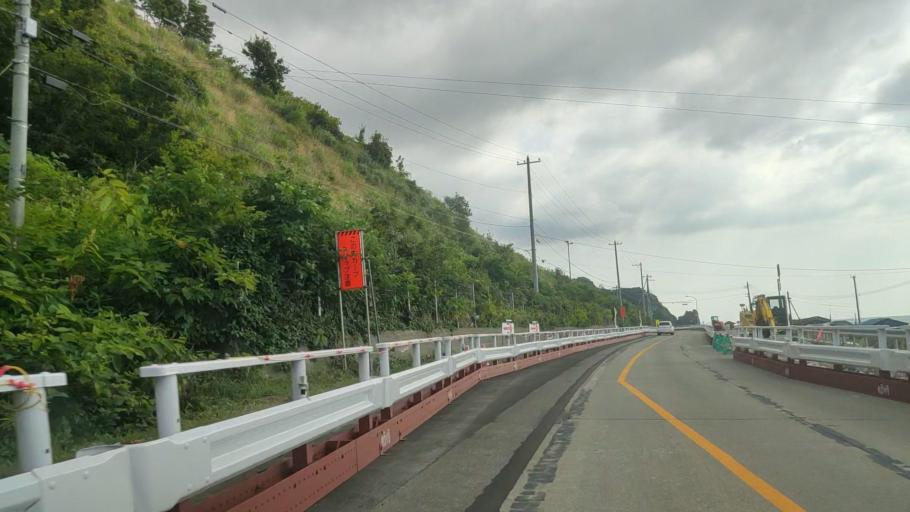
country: JP
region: Hokkaido
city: Rumoi
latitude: 43.7760
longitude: 141.3695
